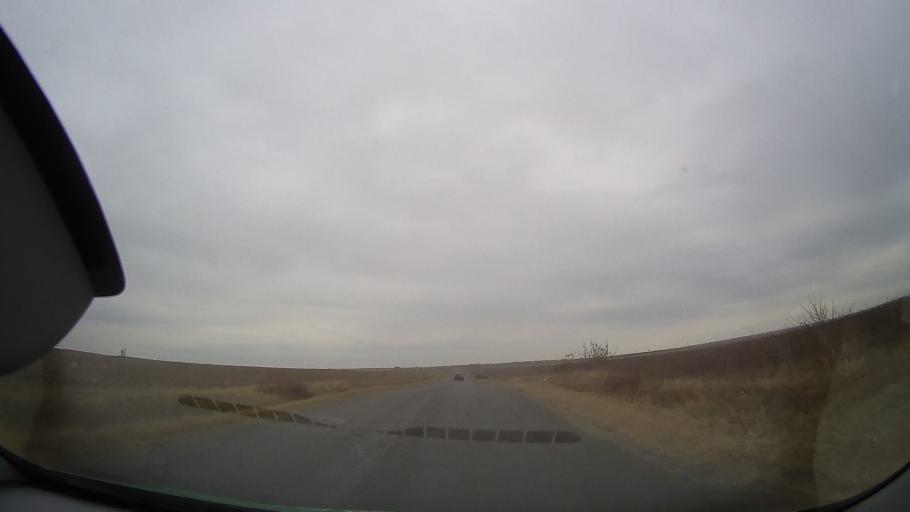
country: RO
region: Buzau
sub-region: Comuna Rusetu
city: Rusetu
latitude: 44.9658
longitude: 27.2011
